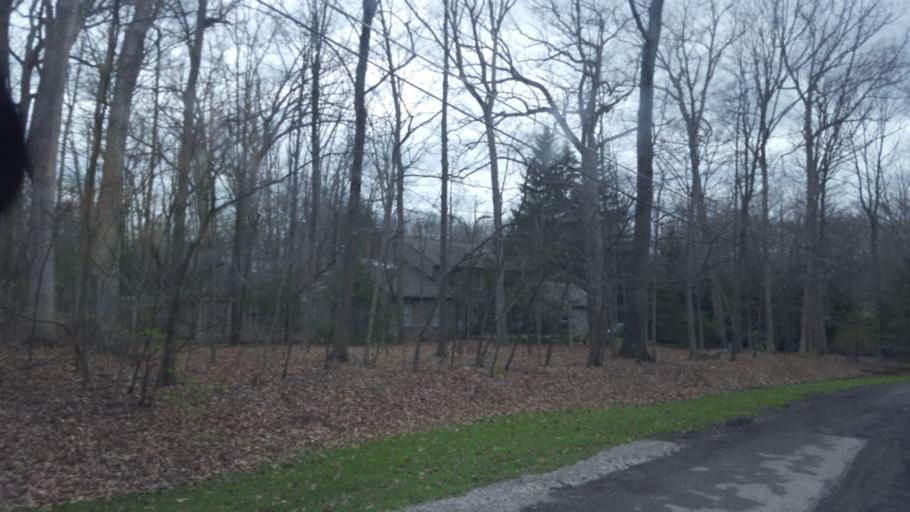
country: US
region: Ohio
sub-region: Franklin County
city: Westerville
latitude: 40.1386
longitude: -82.8633
